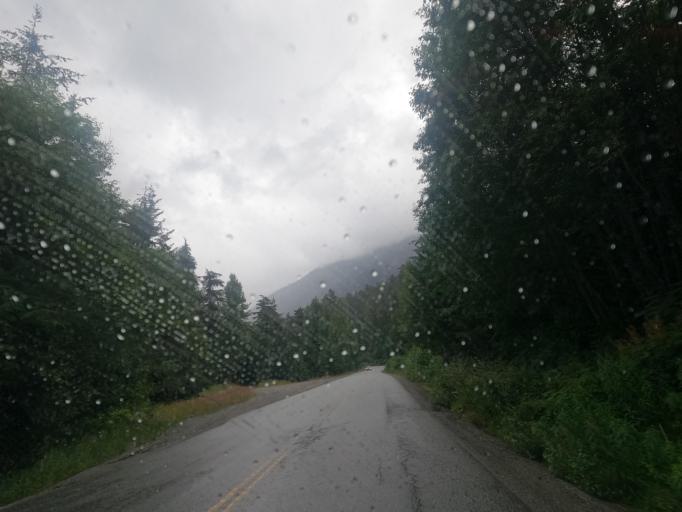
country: CA
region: British Columbia
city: Pemberton
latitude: 50.3366
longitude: -122.5443
